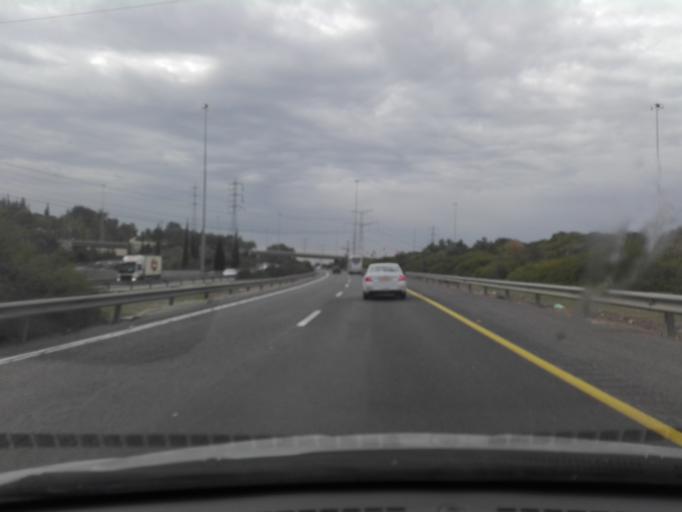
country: IL
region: Central District
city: Lod
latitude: 31.9586
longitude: 34.9369
